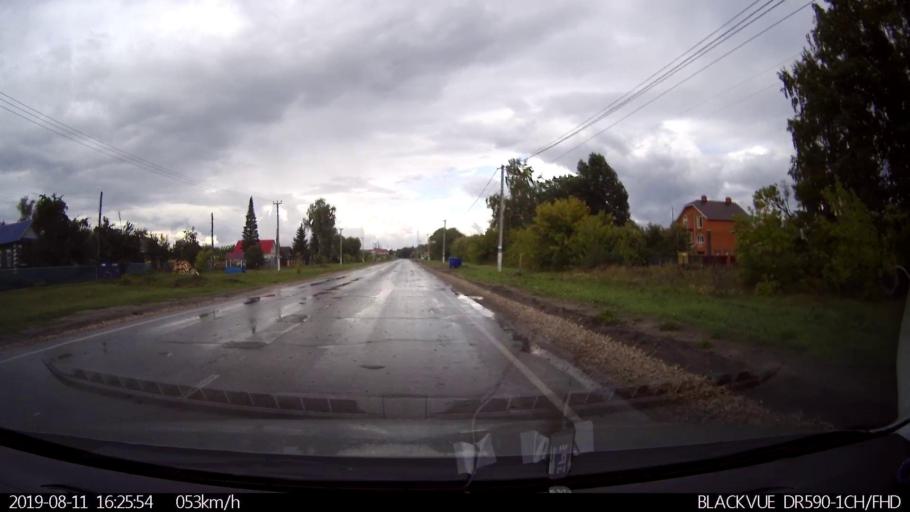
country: RU
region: Ulyanovsk
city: Mayna
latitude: 54.1079
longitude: 47.6101
